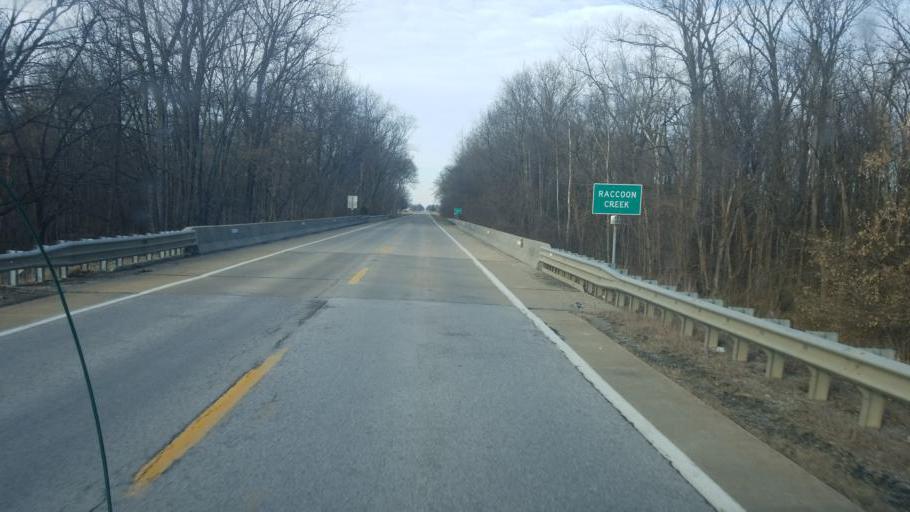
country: US
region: Illinois
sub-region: Lawrence County
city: Bridgeport
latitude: 38.5672
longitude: -87.6946
